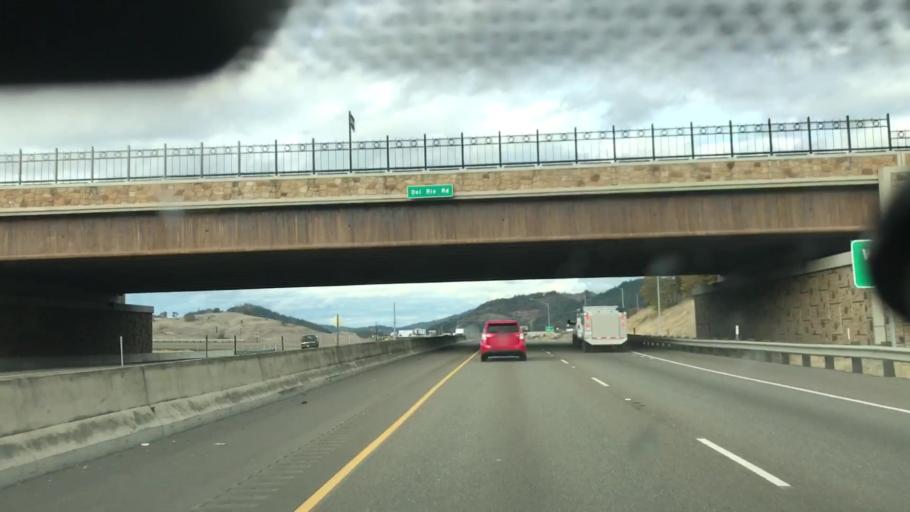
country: US
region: Oregon
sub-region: Douglas County
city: Roseburg North
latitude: 43.2901
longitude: -123.3561
